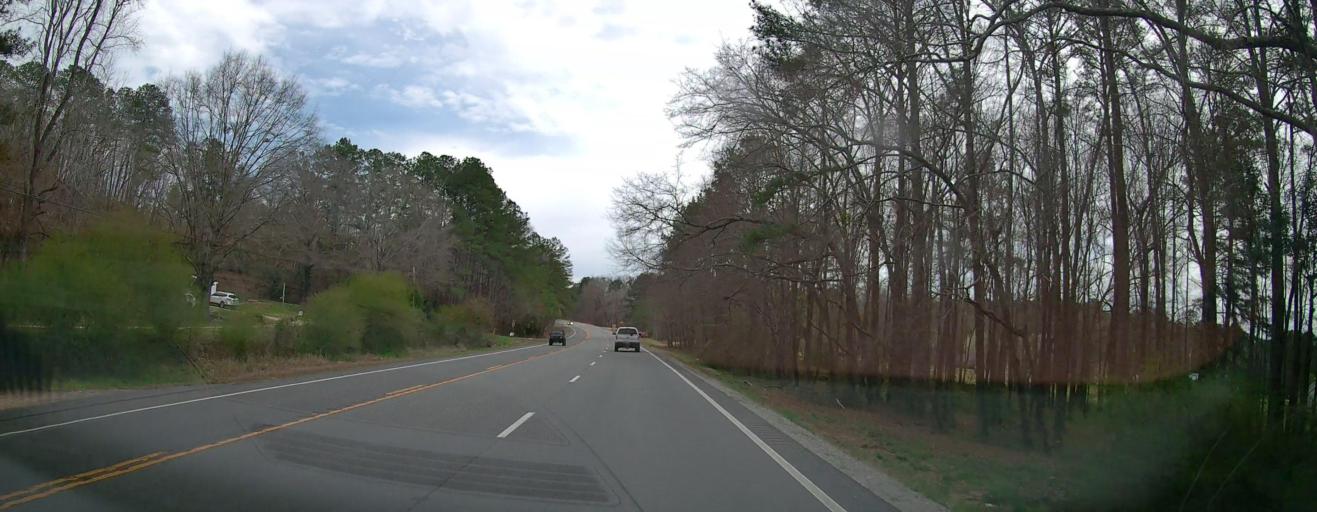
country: US
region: Alabama
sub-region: Marion County
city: Guin
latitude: 33.9919
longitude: -87.9271
